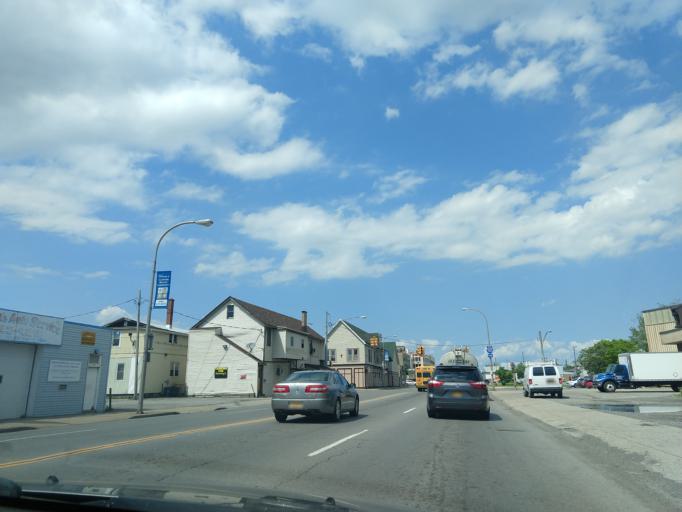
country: US
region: New York
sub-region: Erie County
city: West Seneca
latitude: 42.8715
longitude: -78.8204
